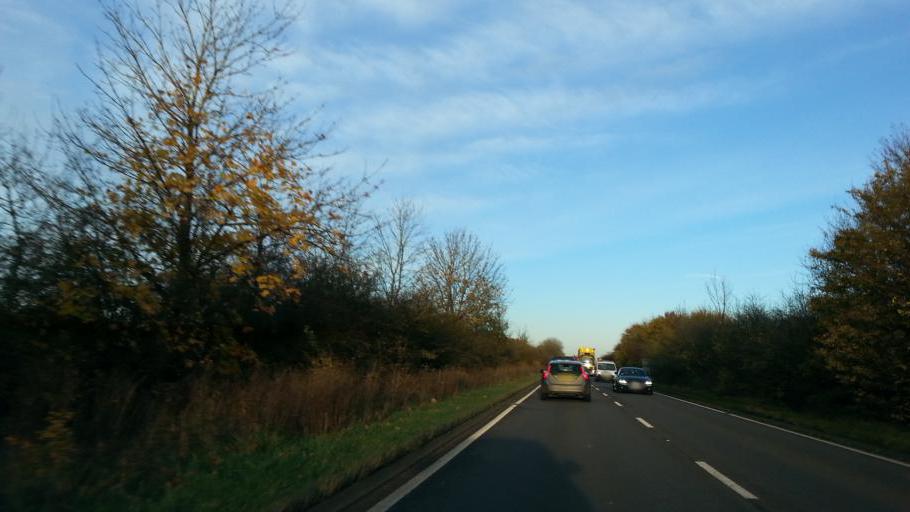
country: GB
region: England
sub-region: Northamptonshire
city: Corby
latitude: 52.5002
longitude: -0.6280
